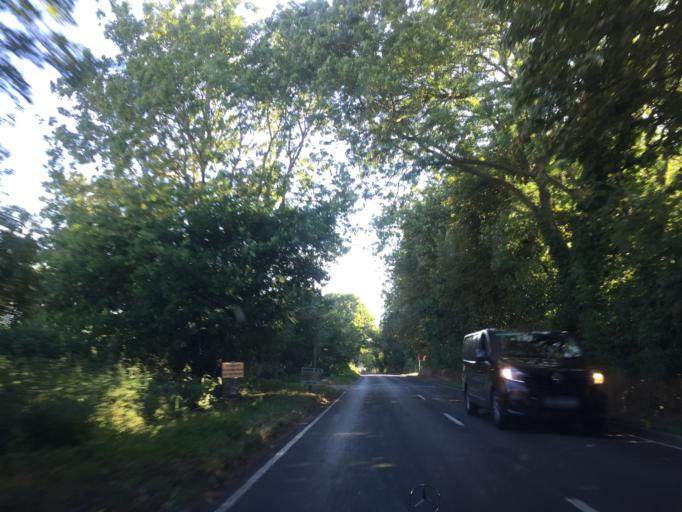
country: GB
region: England
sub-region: Oxfordshire
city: Watlington
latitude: 51.6492
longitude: -1.0001
